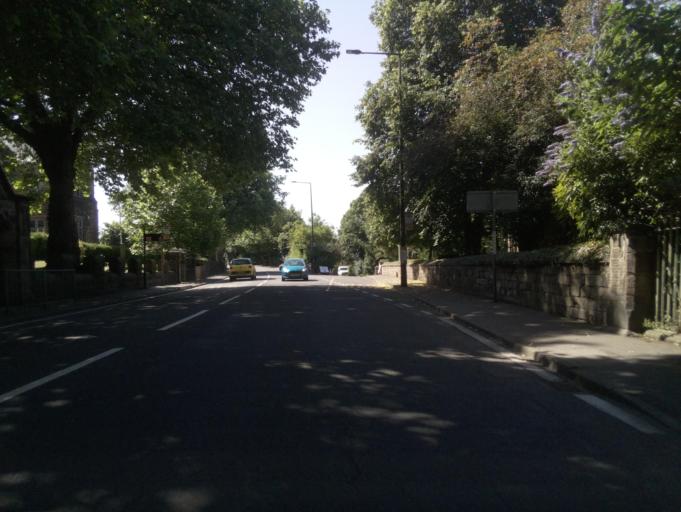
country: GB
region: England
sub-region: Derbyshire
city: Belper
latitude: 53.0189
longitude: -1.4849
